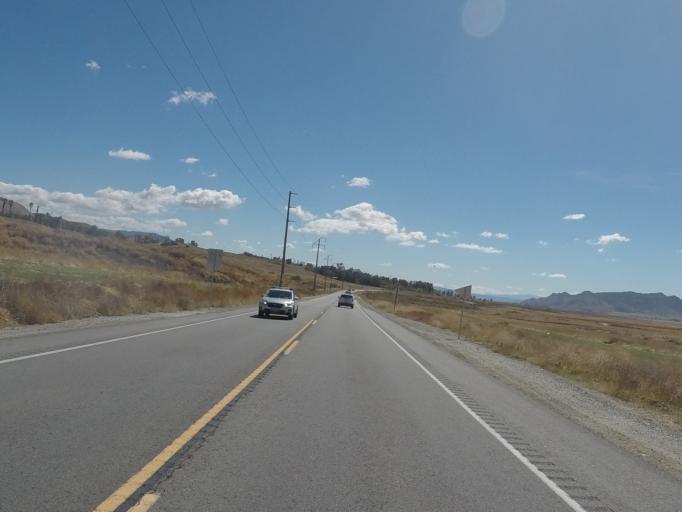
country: US
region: California
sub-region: Riverside County
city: Lakeview
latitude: 33.9014
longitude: -117.0863
